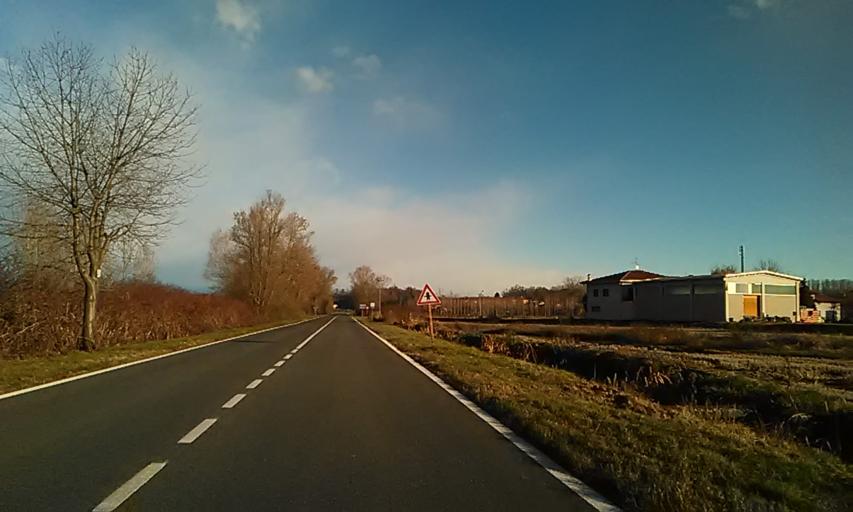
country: IT
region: Piedmont
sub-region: Provincia di Vercelli
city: Buronzo
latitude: 45.4793
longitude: 8.2608
